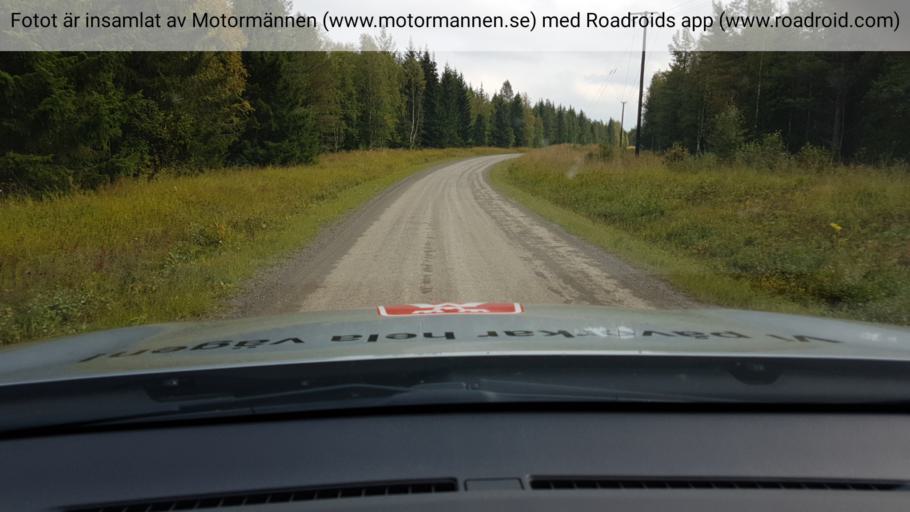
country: SE
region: Jaemtland
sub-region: Stroemsunds Kommun
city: Stroemsund
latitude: 63.7369
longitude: 15.4210
